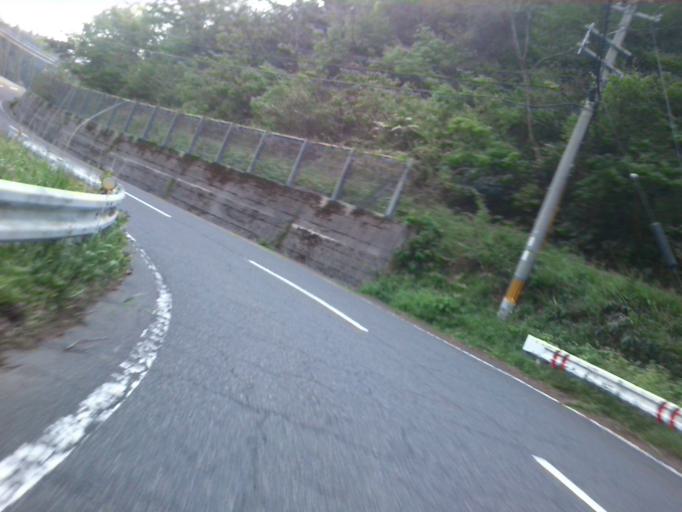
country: JP
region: Kyoto
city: Miyazu
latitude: 35.6923
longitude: 135.1650
